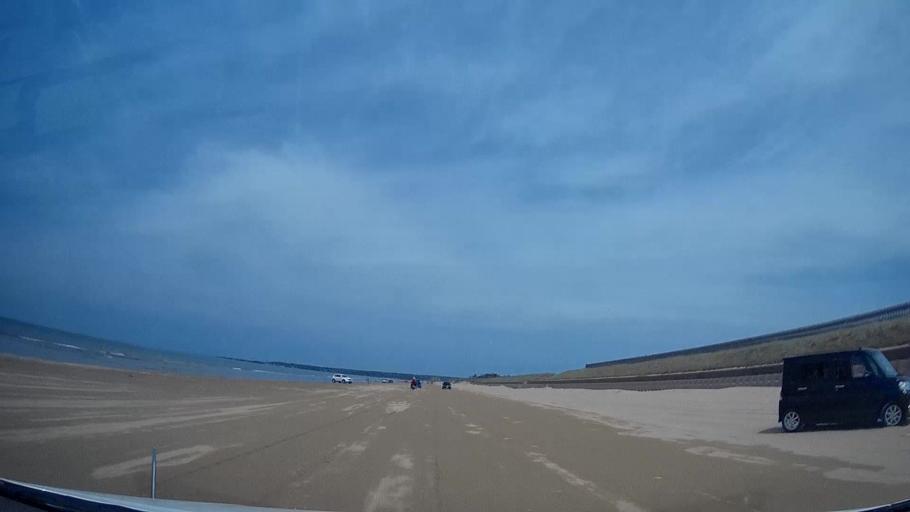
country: JP
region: Ishikawa
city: Hakui
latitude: 36.8784
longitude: 136.7619
